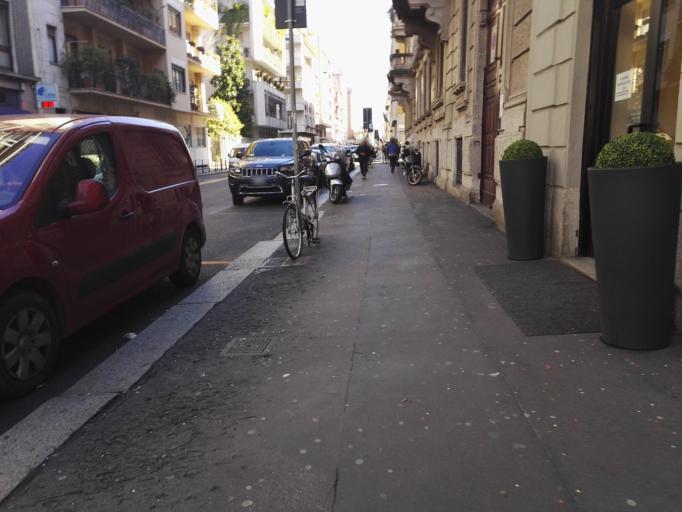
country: IT
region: Lombardy
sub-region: Citta metropolitana di Milano
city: Milano
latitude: 45.4775
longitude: 9.1857
